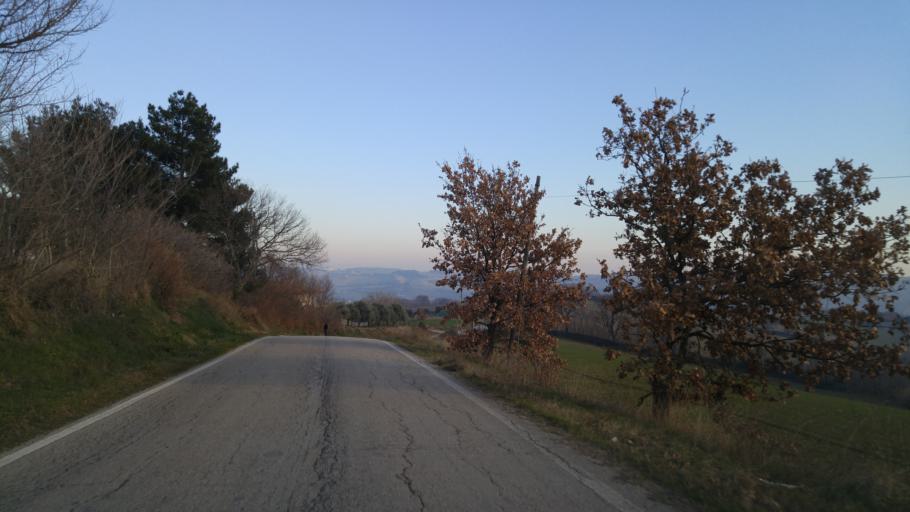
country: IT
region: The Marches
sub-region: Provincia di Pesaro e Urbino
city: Monte Porzio
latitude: 43.6974
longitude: 13.0268
